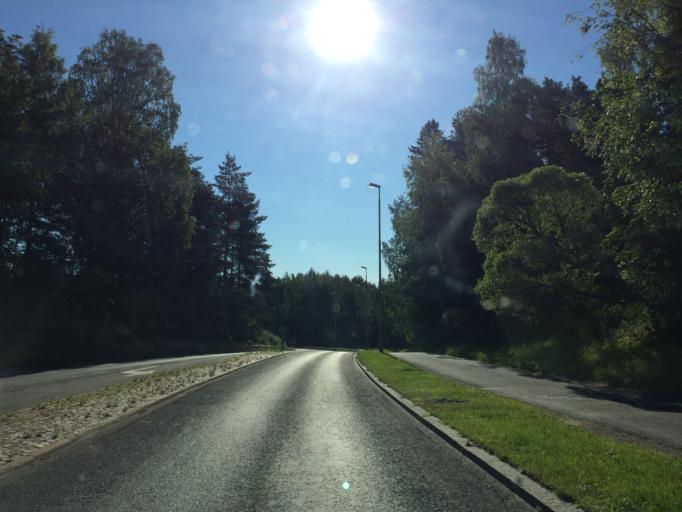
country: FI
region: Haeme
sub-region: Haemeenlinna
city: Haemeenlinna
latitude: 60.9879
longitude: 24.4284
